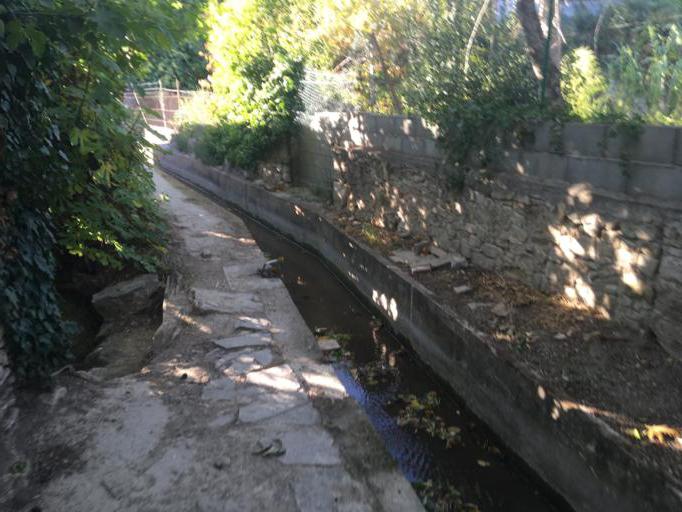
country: FR
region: Provence-Alpes-Cote d'Azur
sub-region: Departement du Var
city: Draguignan
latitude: 43.5439
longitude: 6.4581
